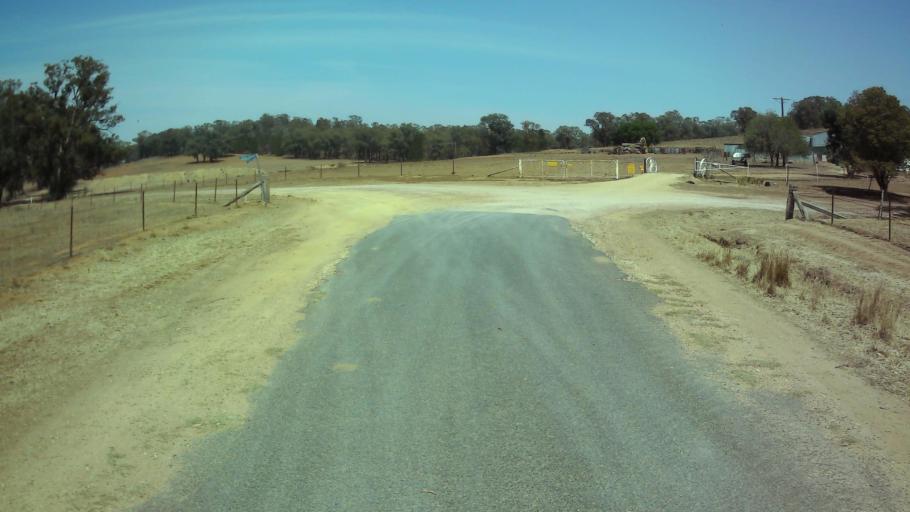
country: AU
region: New South Wales
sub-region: Weddin
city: Grenfell
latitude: -33.8954
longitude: 148.1372
